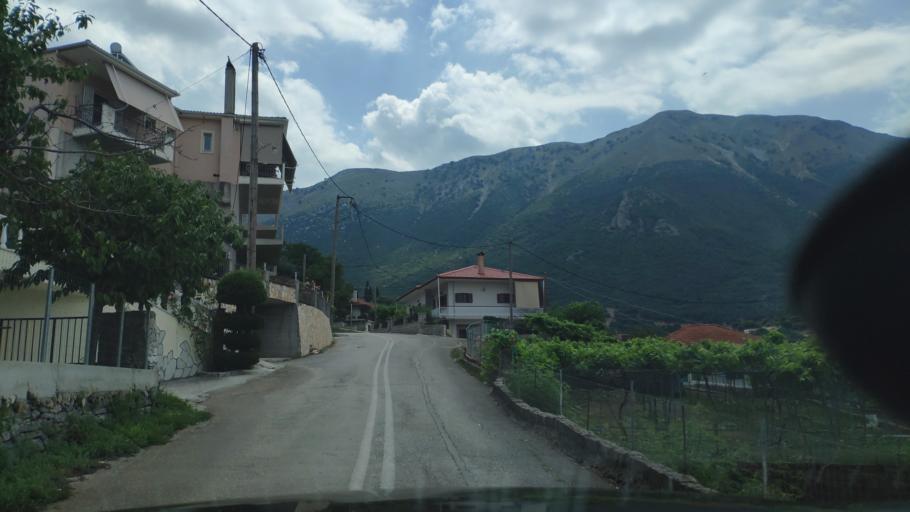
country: GR
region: Epirus
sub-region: Nomos Artas
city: Kampi
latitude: 39.2723
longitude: 20.9388
